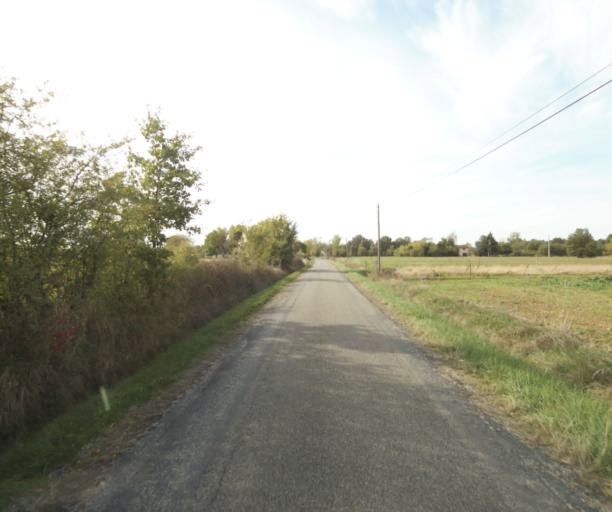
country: FR
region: Midi-Pyrenees
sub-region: Departement du Tarn-et-Garonne
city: Campsas
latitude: 43.9113
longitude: 1.3249
